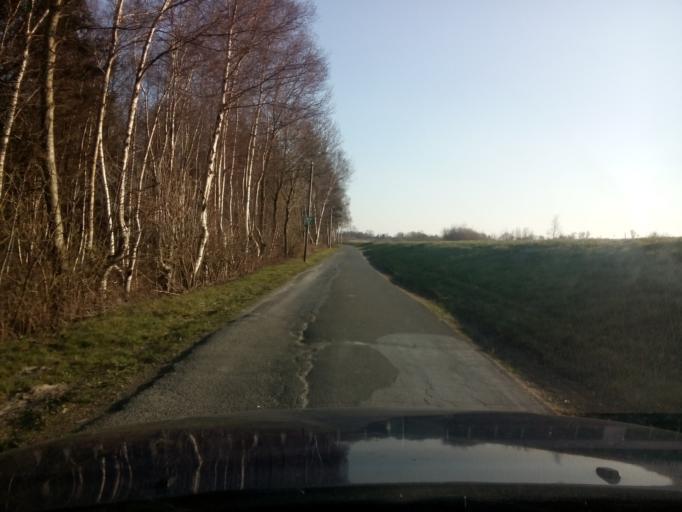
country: DE
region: Lower Saxony
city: Lilienthal
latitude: 53.1518
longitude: 8.8425
